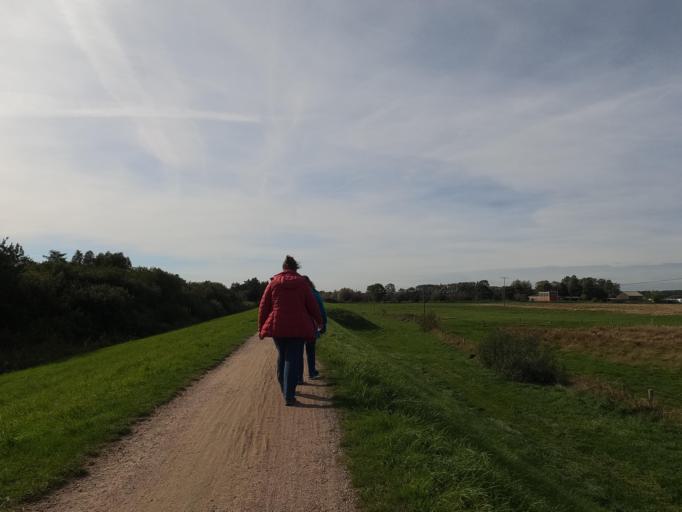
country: DE
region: Schleswig-Holstein
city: Kellenhusen
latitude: 54.1702
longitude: 11.0238
